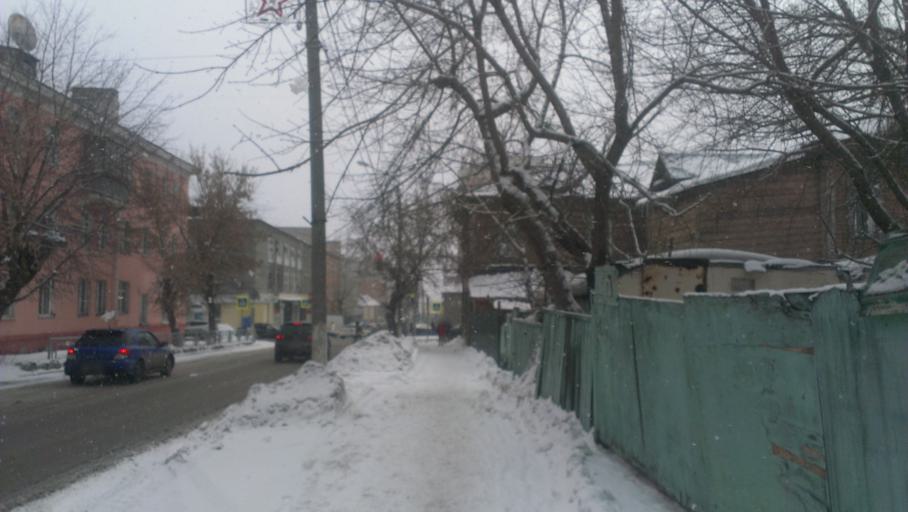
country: RU
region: Altai Krai
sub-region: Gorod Barnaulskiy
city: Barnaul
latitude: 53.3349
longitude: 83.7855
